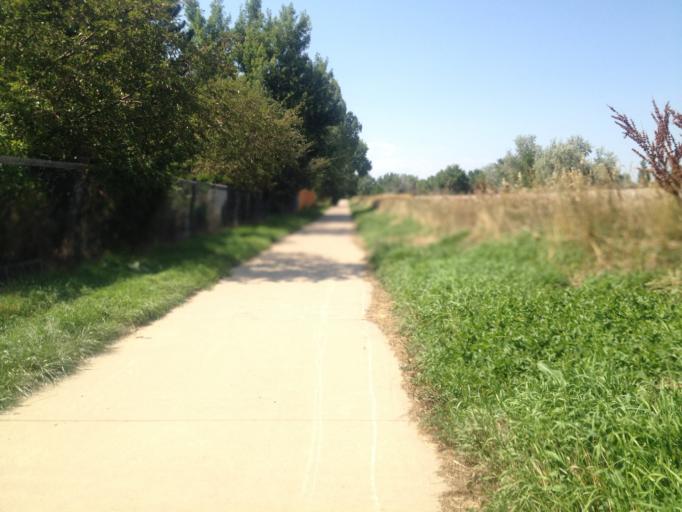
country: US
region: Colorado
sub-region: Boulder County
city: Louisville
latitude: 39.9924
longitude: -105.1362
